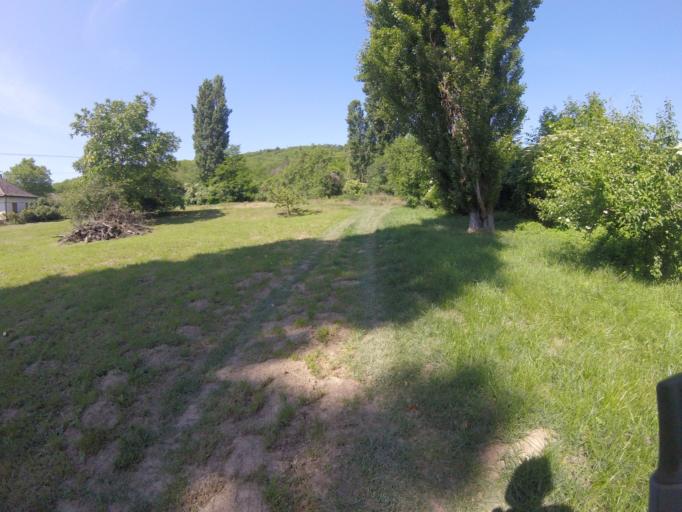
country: HU
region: Zala
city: Zalaszentgrot
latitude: 46.9211
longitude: 17.0539
